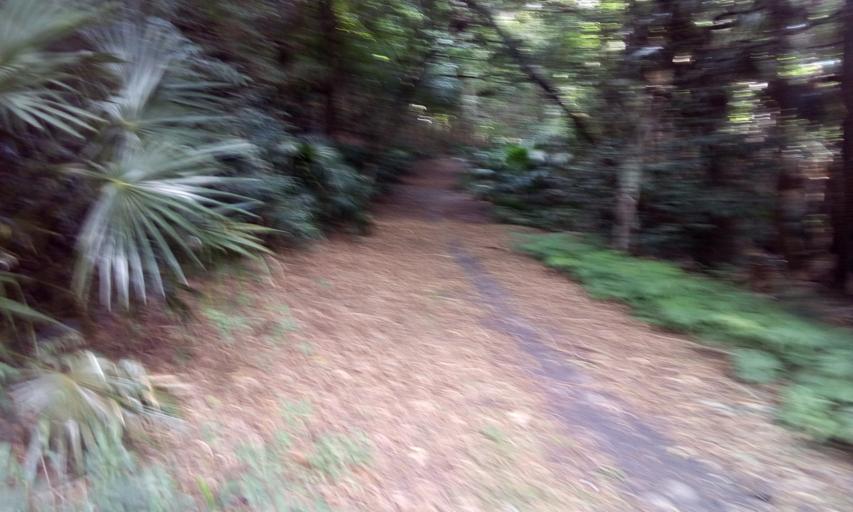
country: AU
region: New South Wales
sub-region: Wollongong
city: Cordeaux Heights
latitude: -34.4411
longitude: 150.8129
